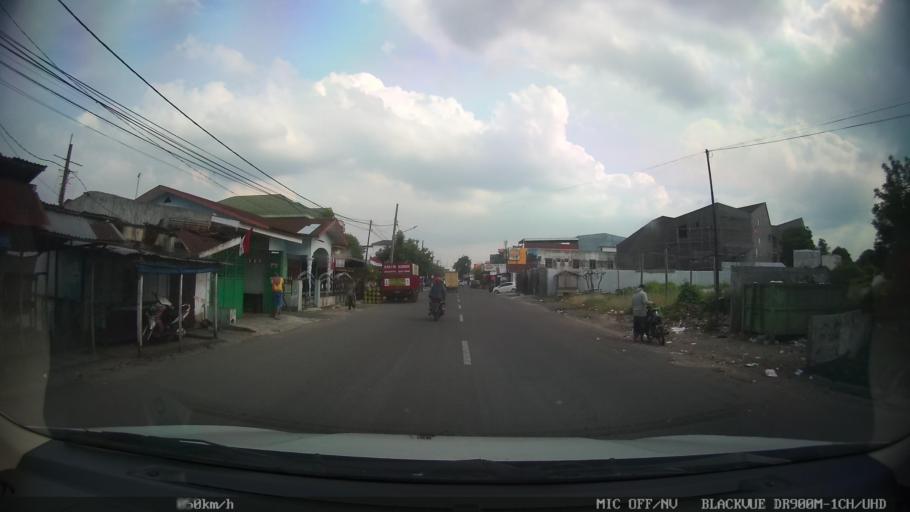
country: ID
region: North Sumatra
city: Binjai
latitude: 3.6019
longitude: 98.4892
